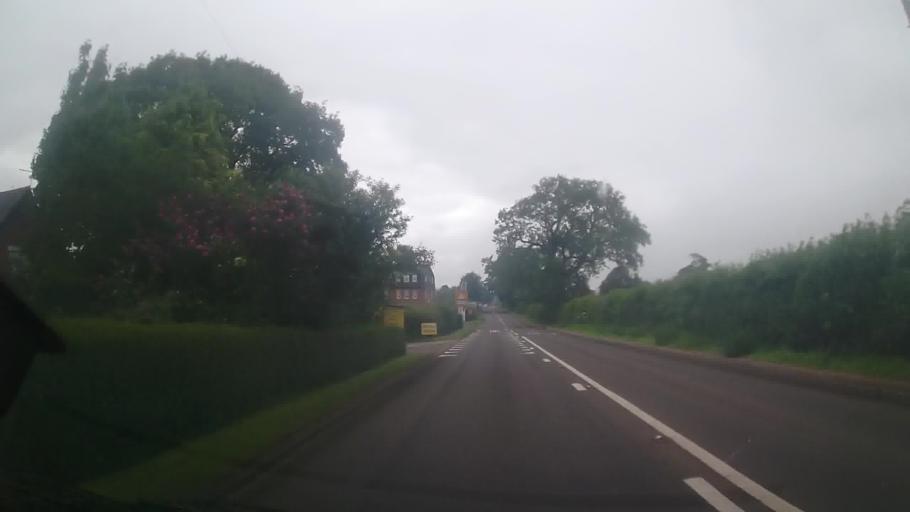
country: GB
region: England
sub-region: Shropshire
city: Whitchurch
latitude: 52.9548
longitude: -2.6722
